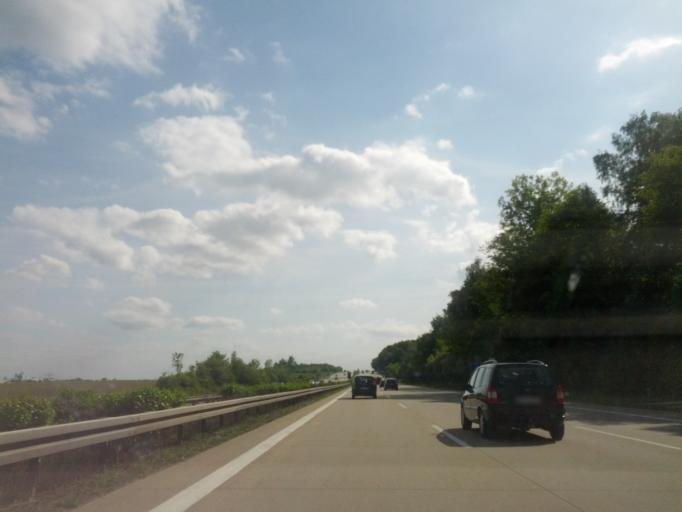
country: DE
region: Saxony
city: Rossau
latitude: 50.9718
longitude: 13.0845
